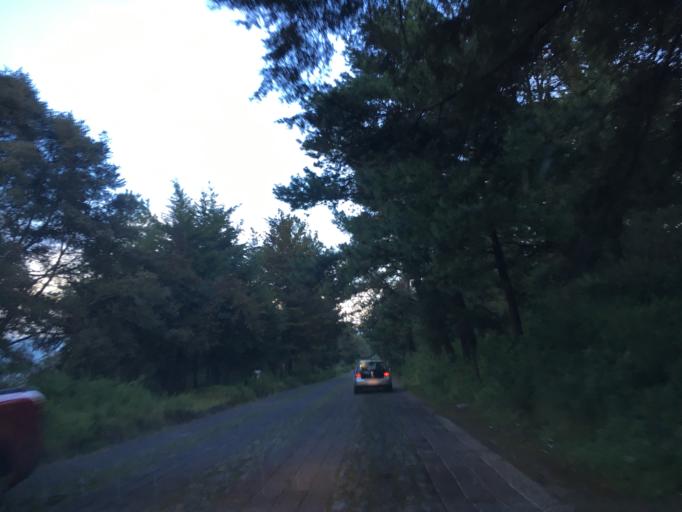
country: MX
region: Michoacan
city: Villa Escalante
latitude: 19.4134
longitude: -101.6808
